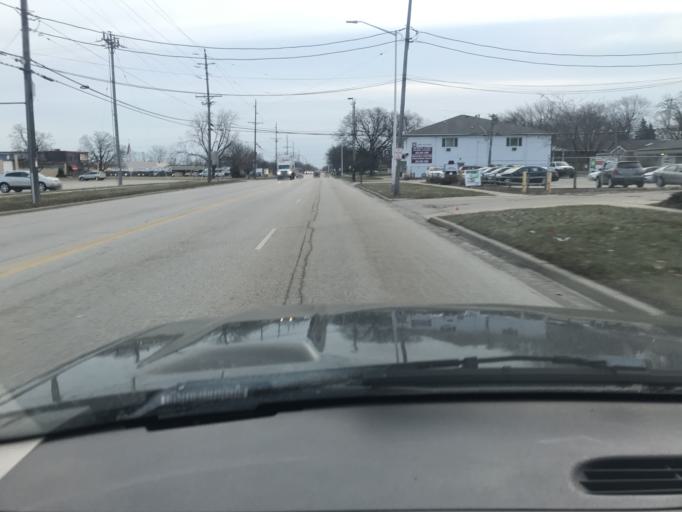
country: US
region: Wisconsin
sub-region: Kenosha County
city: Kenosha
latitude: 42.5887
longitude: -87.8790
